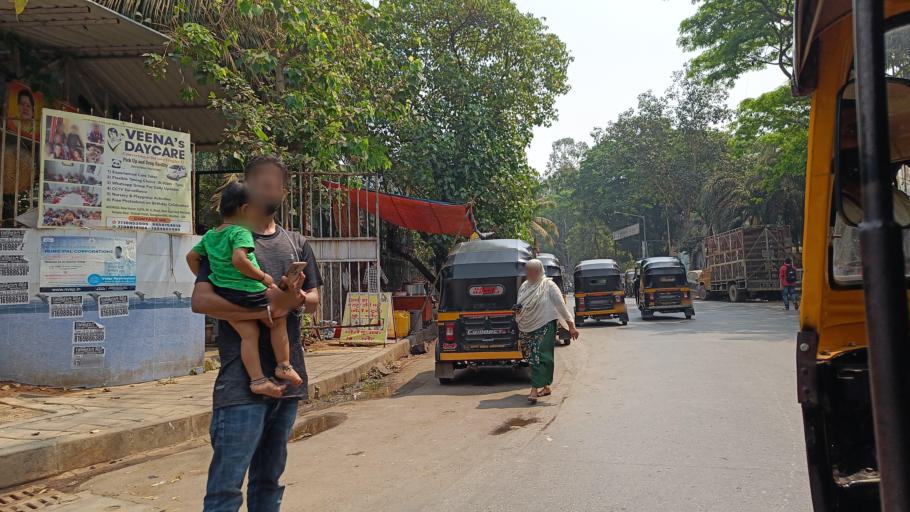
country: IN
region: Maharashtra
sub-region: Mumbai Suburban
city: Powai
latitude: 19.1533
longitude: 72.8396
